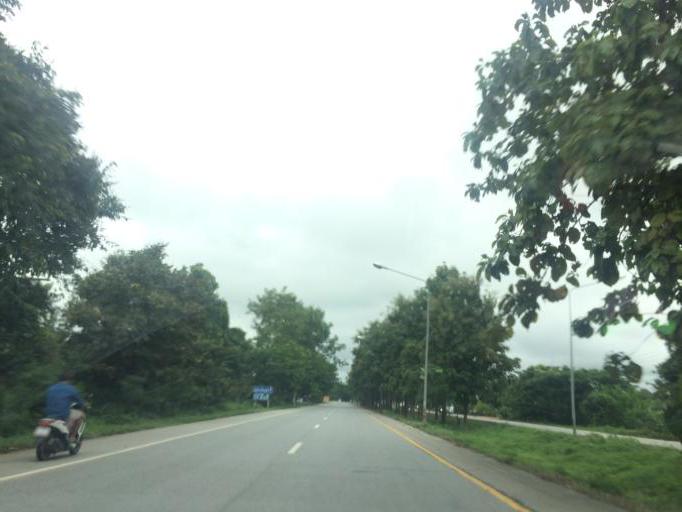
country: TH
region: Chiang Rai
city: Mae Lao
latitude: 19.8035
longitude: 99.7541
